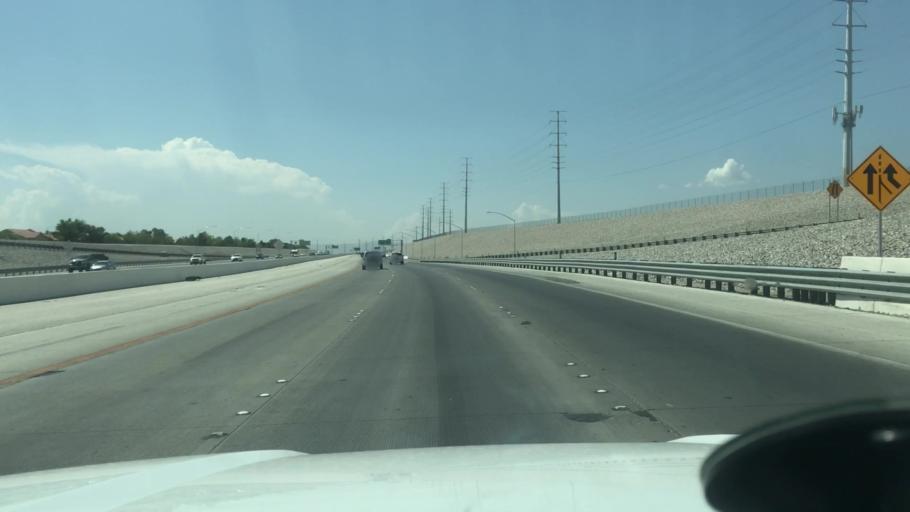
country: US
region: Nevada
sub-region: Clark County
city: Summerlin South
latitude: 36.2052
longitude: -115.3409
